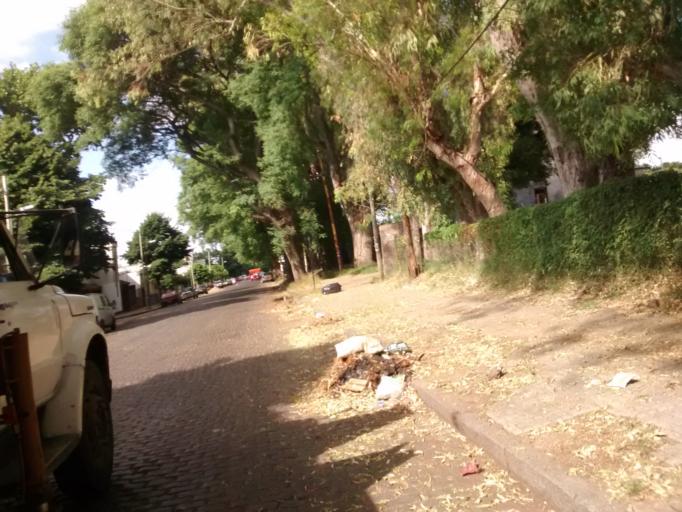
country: AR
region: Buenos Aires
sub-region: Partido de La Plata
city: La Plata
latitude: -34.9372
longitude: -57.9366
